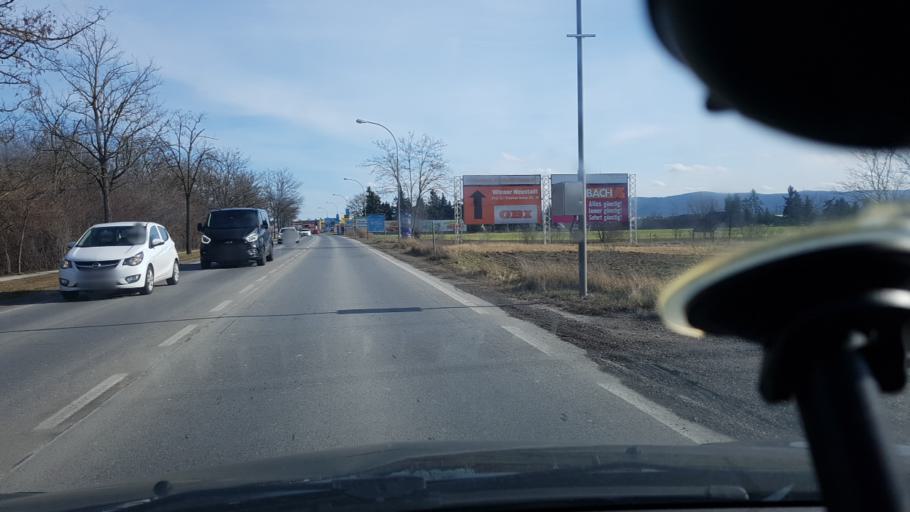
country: AT
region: Lower Austria
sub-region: Wiener Neustadt Stadt
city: Wiener Neustadt
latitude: 47.8061
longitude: 16.2073
